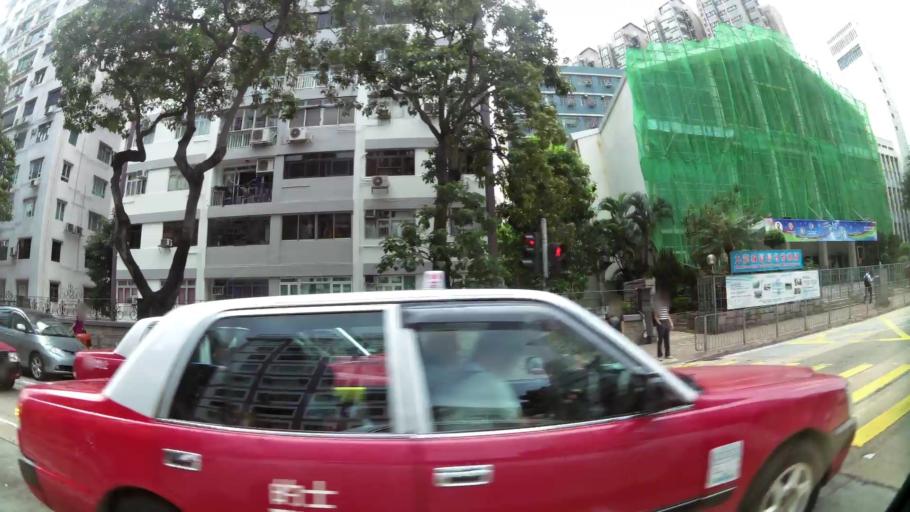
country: HK
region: Kowloon City
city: Kowloon
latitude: 22.3249
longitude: 114.1859
